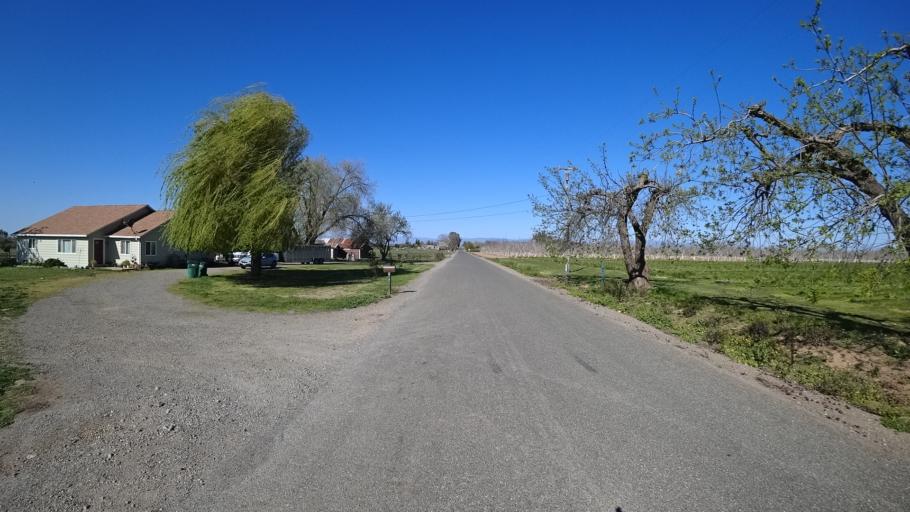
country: US
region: California
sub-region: Glenn County
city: Orland
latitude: 39.7369
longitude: -122.2334
